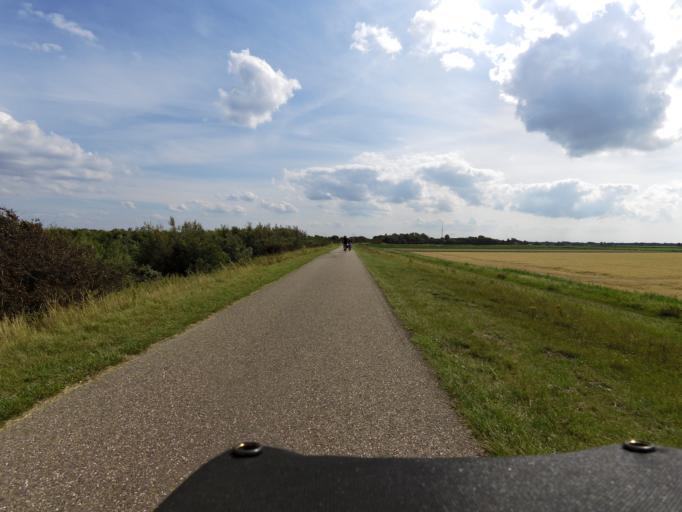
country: NL
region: South Holland
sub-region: Gemeente Goeree-Overflakkee
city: Ouddorp
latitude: 51.8186
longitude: 3.8963
